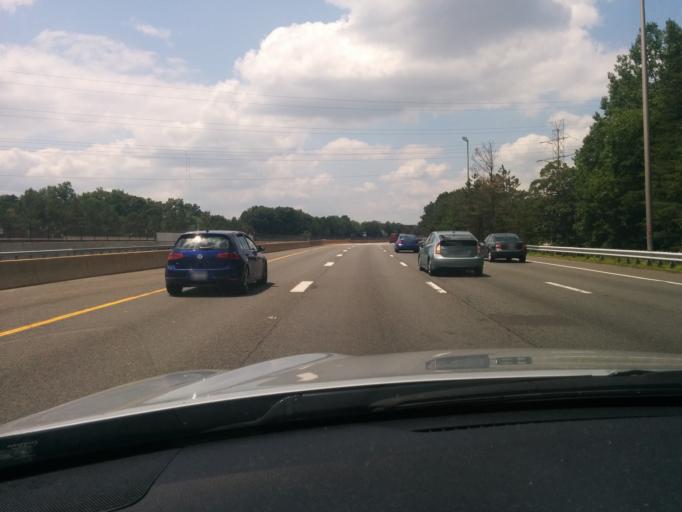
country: US
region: Virginia
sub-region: Fairfax County
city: Reston
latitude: 38.9450
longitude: -77.3242
